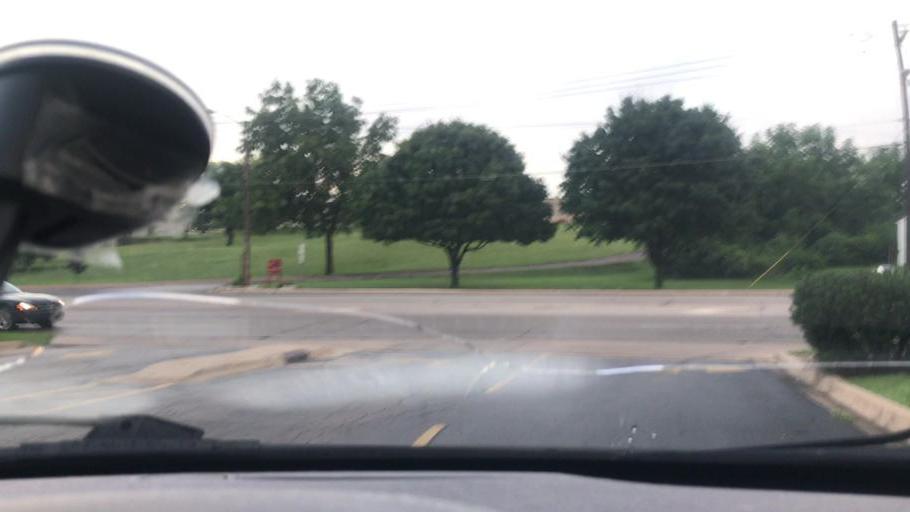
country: US
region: Illinois
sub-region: Tazewell County
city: Pekin
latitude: 40.5598
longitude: -89.6197
